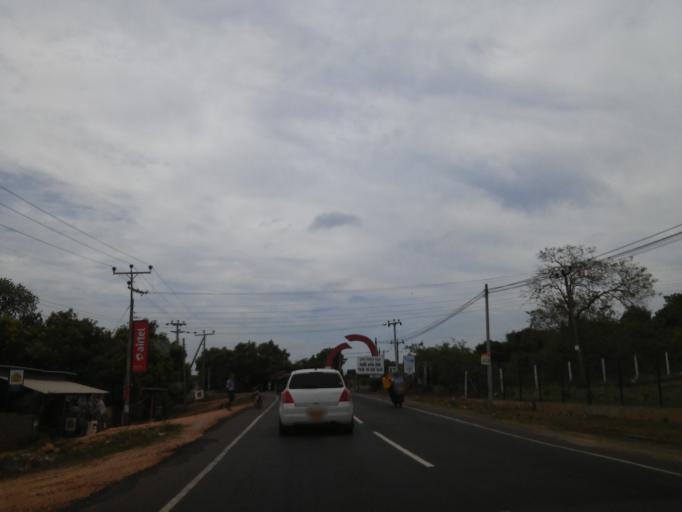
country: LK
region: Eastern Province
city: Trincomalee
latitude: 8.6405
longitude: 81.2024
